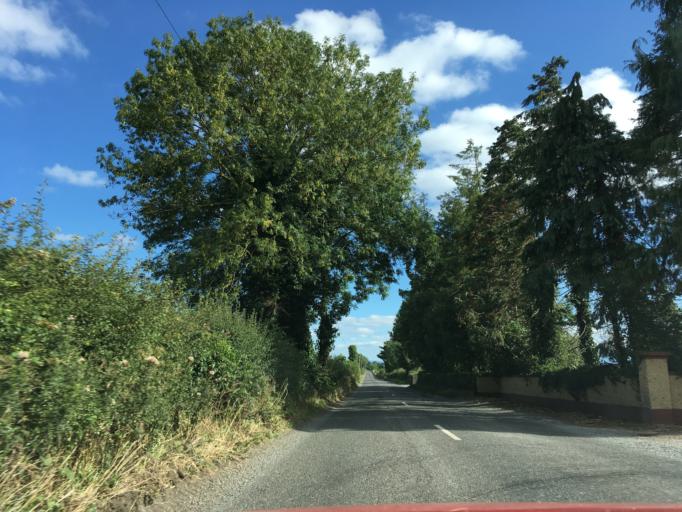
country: IE
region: Munster
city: Cashel
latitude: 52.4722
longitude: -7.9233
